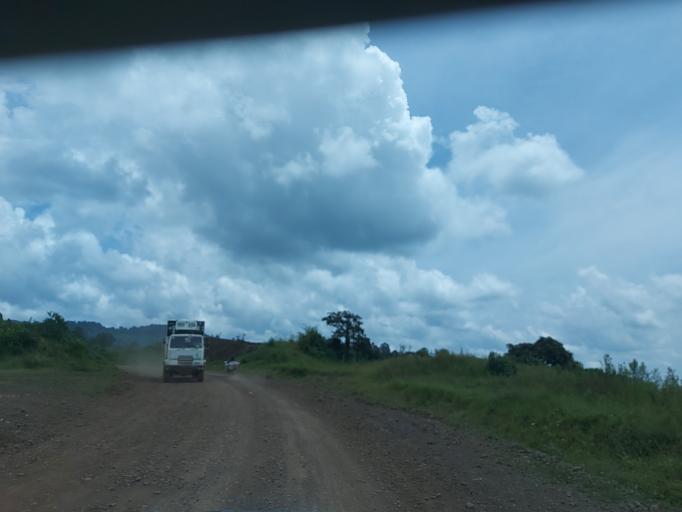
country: CD
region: South Kivu
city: Kabare
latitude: -2.3188
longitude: 28.7631
